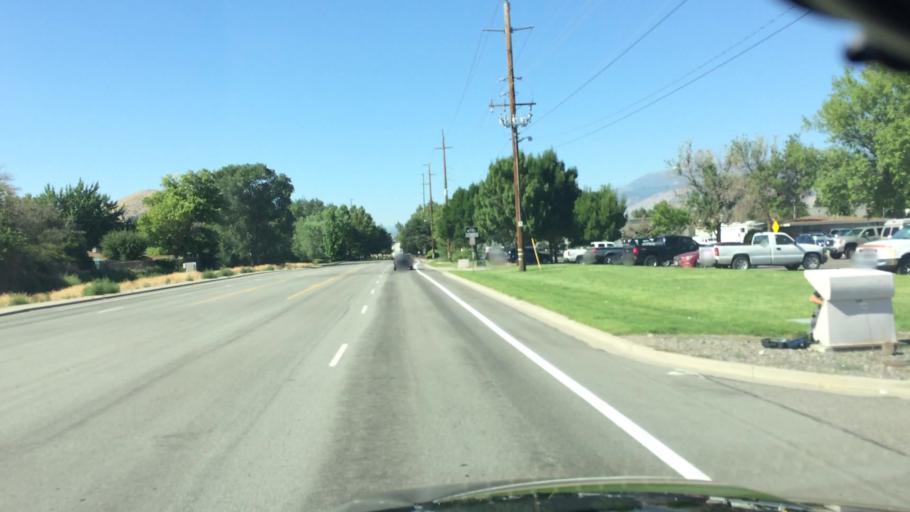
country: US
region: Nevada
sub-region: Washoe County
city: Sparks
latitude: 39.4922
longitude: -119.7560
